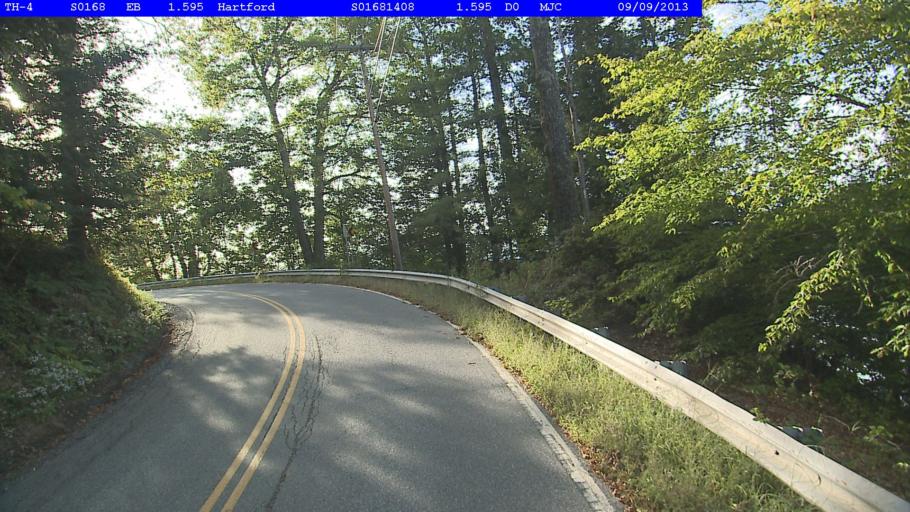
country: US
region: Vermont
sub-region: Windsor County
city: White River Junction
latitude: 43.6421
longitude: -72.4025
